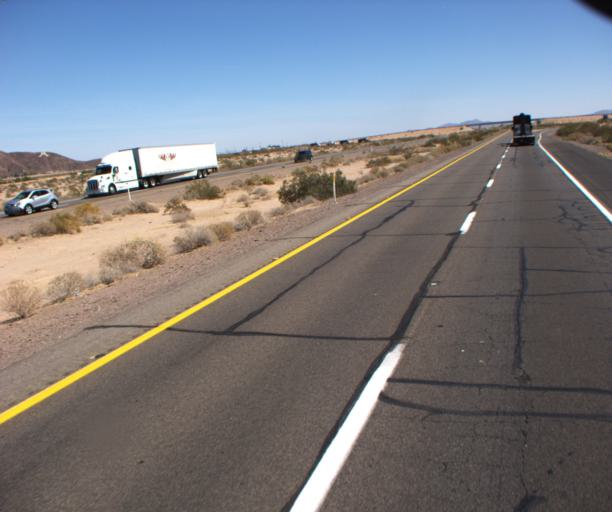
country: US
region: Arizona
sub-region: Yuma County
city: Wellton
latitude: 32.6799
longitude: -114.0292
